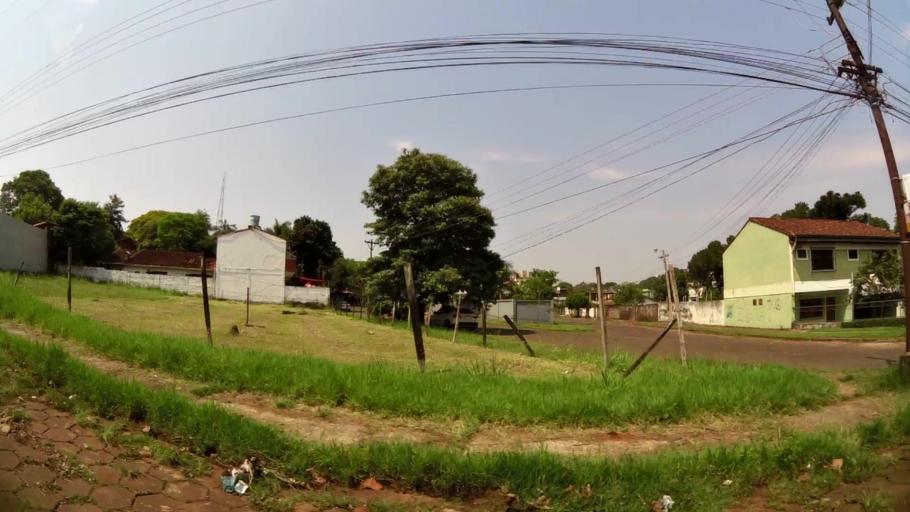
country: PY
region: Alto Parana
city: Ciudad del Este
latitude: -25.5183
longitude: -54.6159
